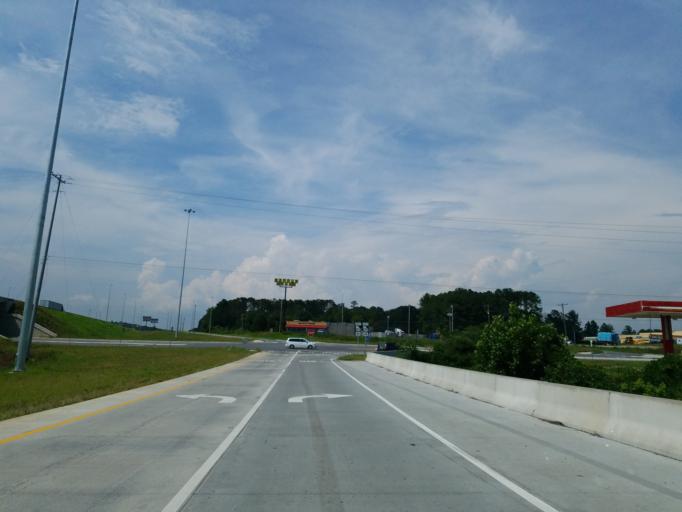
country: US
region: Georgia
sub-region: Gordon County
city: Calhoun
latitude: 34.5108
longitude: -84.9178
